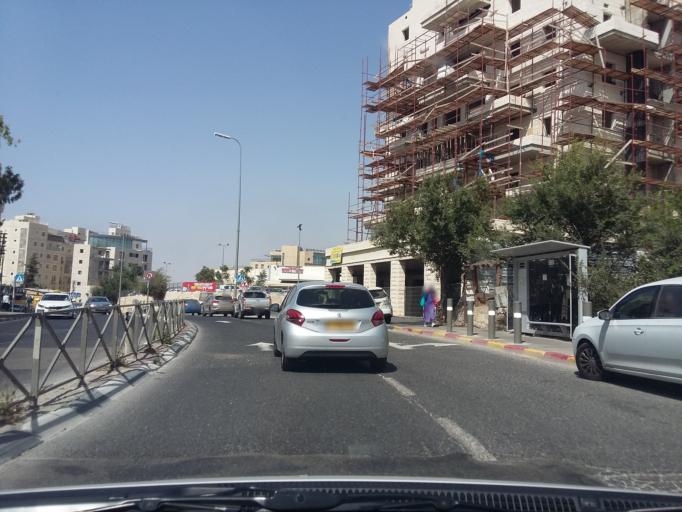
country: IL
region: Jerusalem
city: West Jerusalem
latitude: 31.7911
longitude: 35.2032
